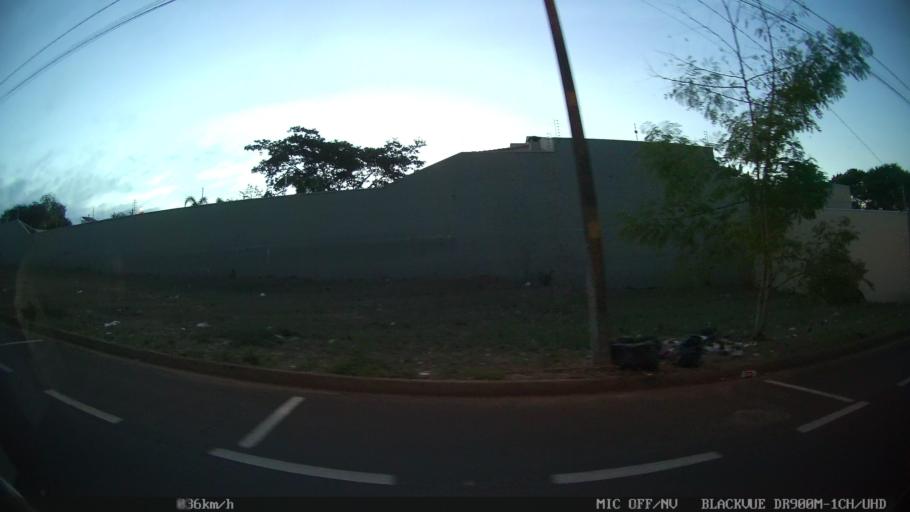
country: BR
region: Sao Paulo
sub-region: Catanduva
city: Catanduva
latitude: -21.1486
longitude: -48.9931
